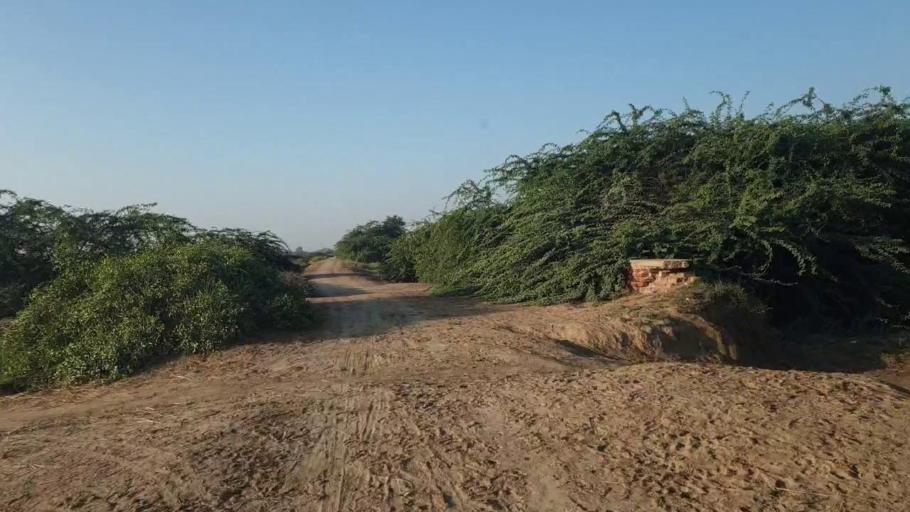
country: PK
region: Sindh
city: Badin
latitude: 24.6276
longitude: 68.7958
